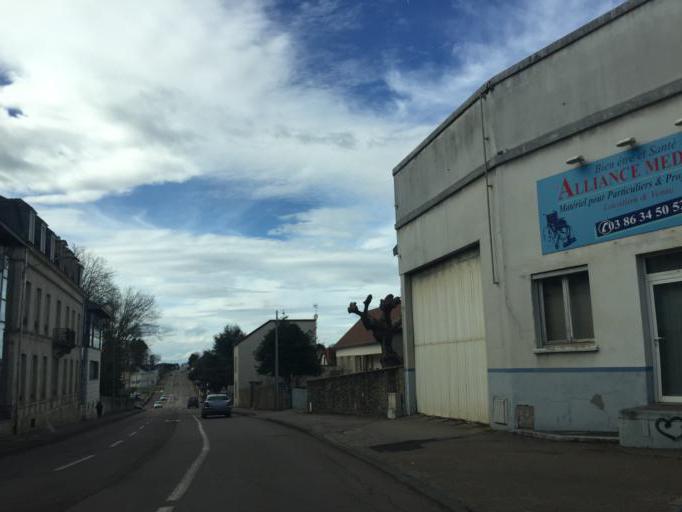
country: FR
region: Bourgogne
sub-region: Departement de l'Yonne
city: Avallon
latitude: 47.4930
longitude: 3.9076
